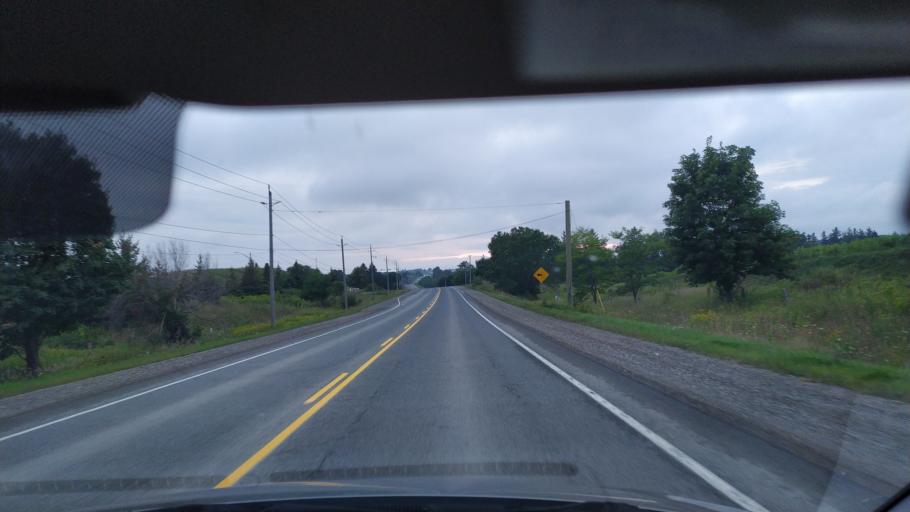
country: CA
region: Ontario
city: Cambridge
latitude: 43.3377
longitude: -80.4118
